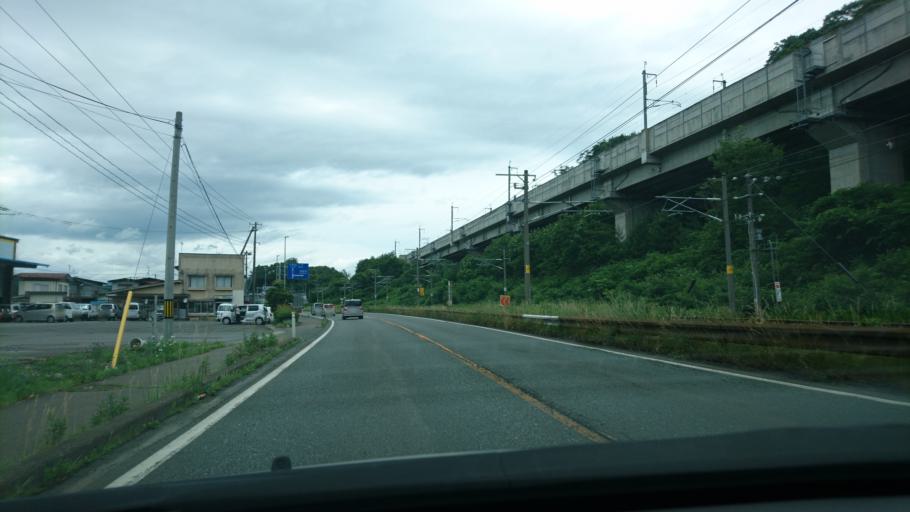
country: JP
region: Iwate
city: Morioka-shi
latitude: 39.9490
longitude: 141.2177
